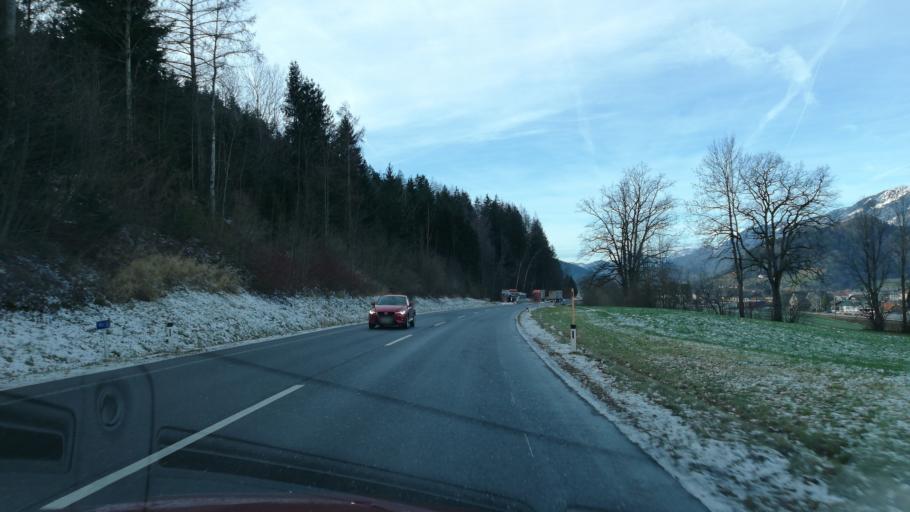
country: AT
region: Upper Austria
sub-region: Politischer Bezirk Kirchdorf an der Krems
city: Rossleithen
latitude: 47.7123
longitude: 14.3322
